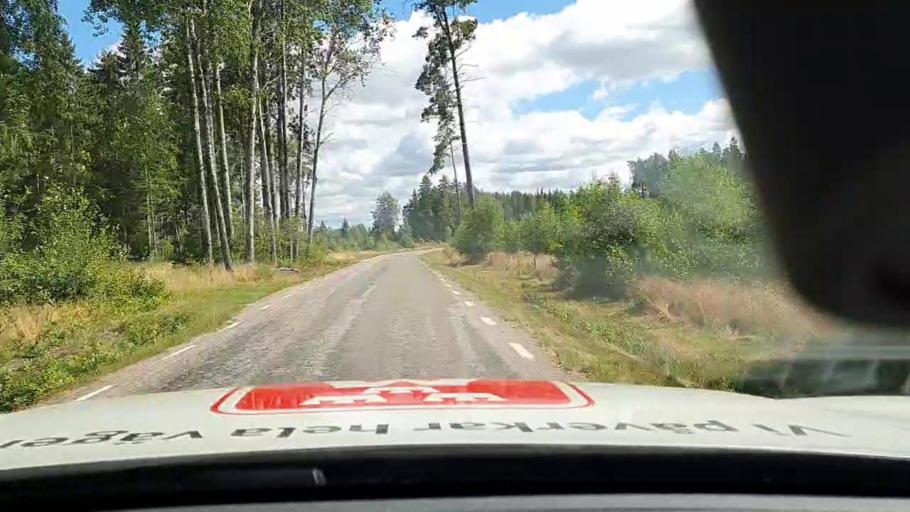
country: SE
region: Vaestra Goetaland
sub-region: Toreboda Kommun
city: Toereboda
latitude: 58.5684
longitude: 14.1354
